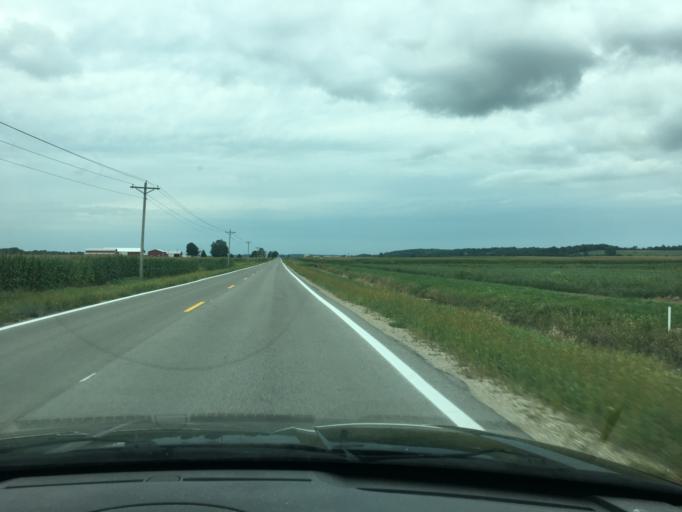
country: US
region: Ohio
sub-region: Champaign County
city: Urbana
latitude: 40.1612
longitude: -83.7842
